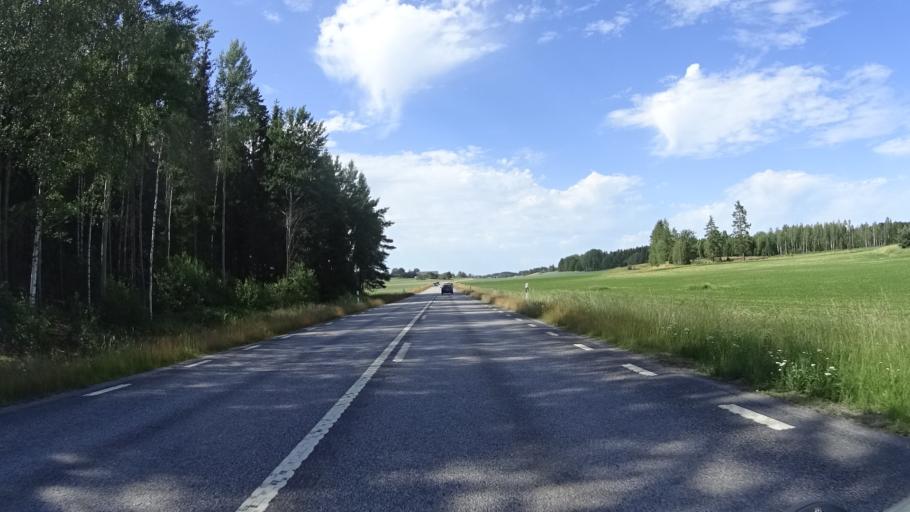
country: SE
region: OEstergoetland
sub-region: Linkopings Kommun
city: Sturefors
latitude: 58.3310
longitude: 15.8543
